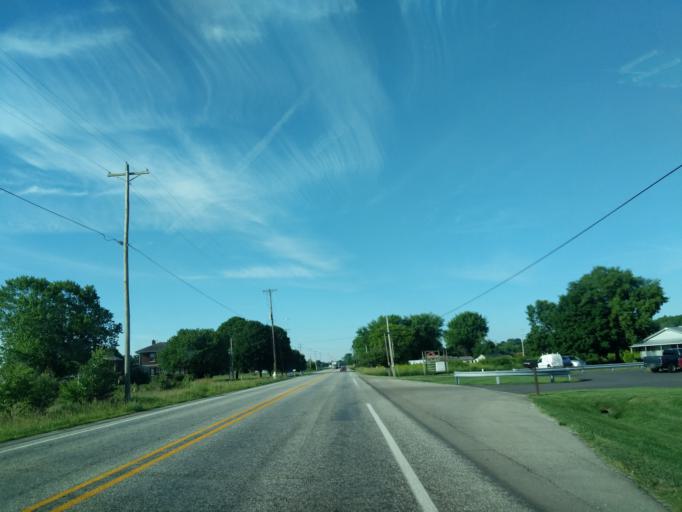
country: US
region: Indiana
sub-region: Madison County
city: Pendleton
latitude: 39.9791
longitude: -85.7538
